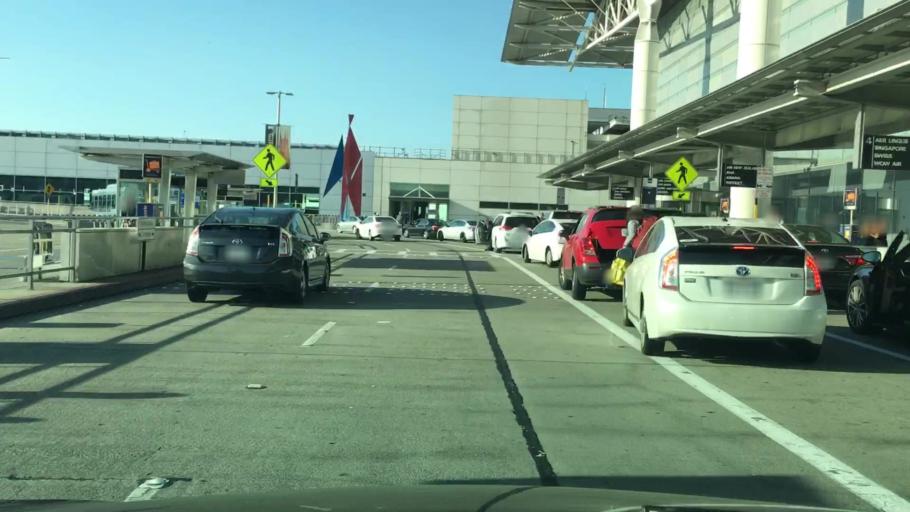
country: US
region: California
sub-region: San Mateo County
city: Millbrae
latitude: 37.6156
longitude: -122.3900
